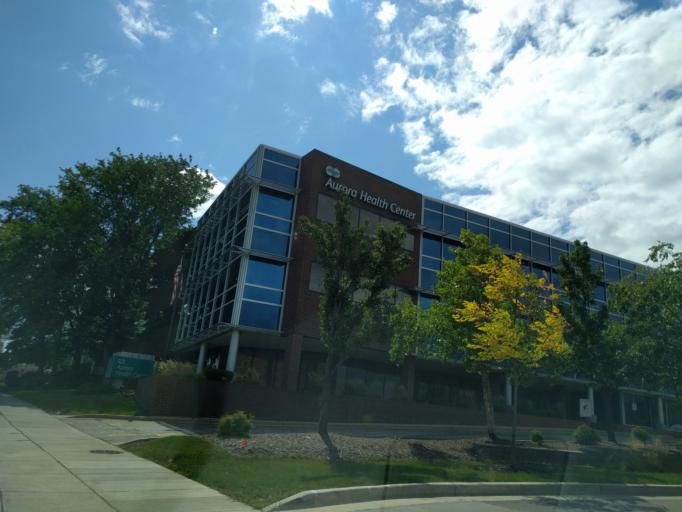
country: US
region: Wisconsin
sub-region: Waukesha County
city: Elm Grove
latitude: 43.0440
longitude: -88.0474
